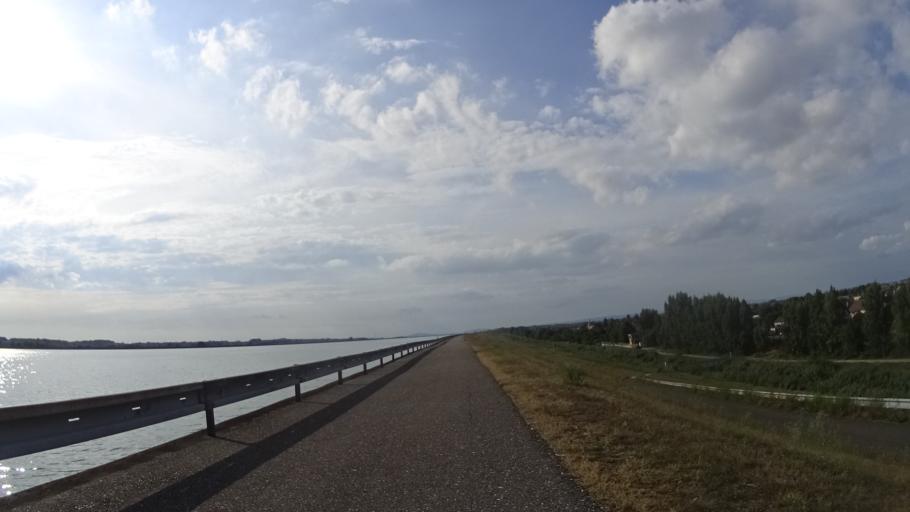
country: HU
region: Gyor-Moson-Sopron
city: Asvanyraro
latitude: 47.9456
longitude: 17.4460
